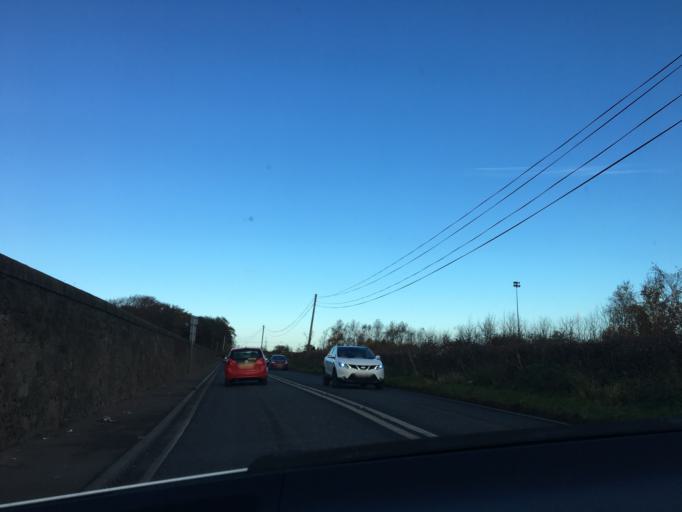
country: GB
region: Scotland
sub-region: Midlothian
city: Dalkeith
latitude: 55.9021
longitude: -3.0504
